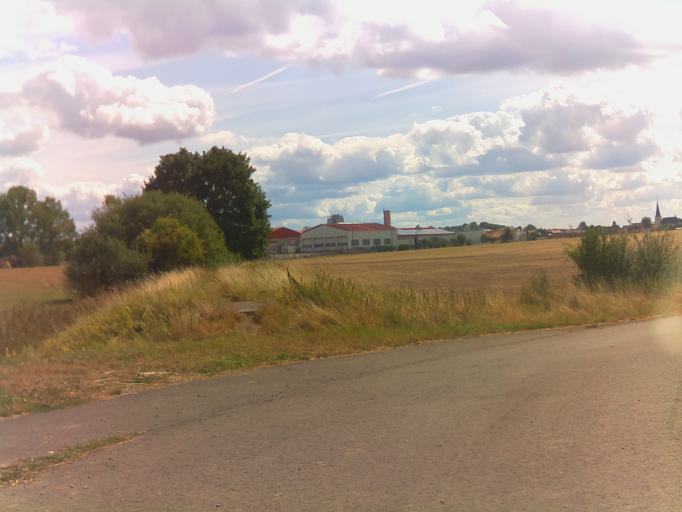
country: DE
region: Thuringia
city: Wolfershausen
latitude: 50.4418
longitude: 10.4572
